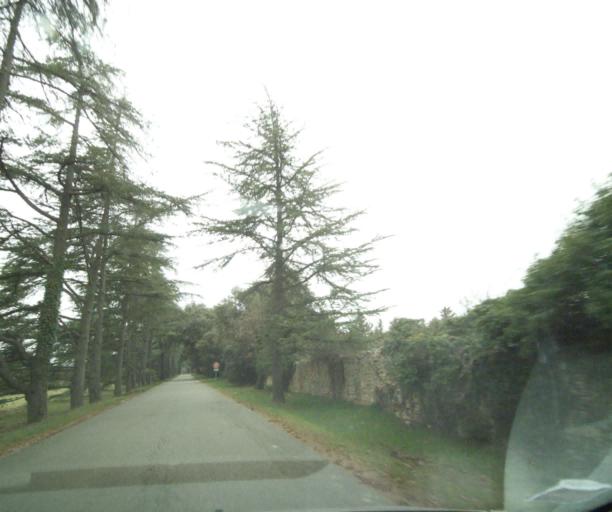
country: FR
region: Provence-Alpes-Cote d'Azur
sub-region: Departement du Var
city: Vinon-sur-Verdon
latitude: 43.7128
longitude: 5.7568
